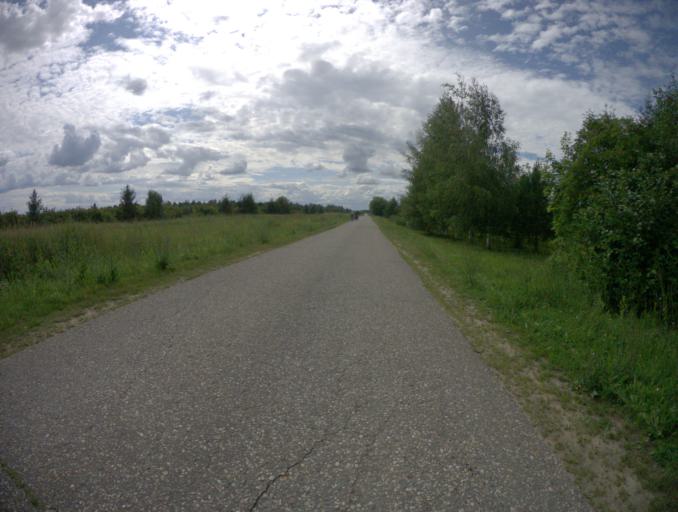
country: RU
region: Vladimir
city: Orgtrud
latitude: 56.3185
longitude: 40.6346
